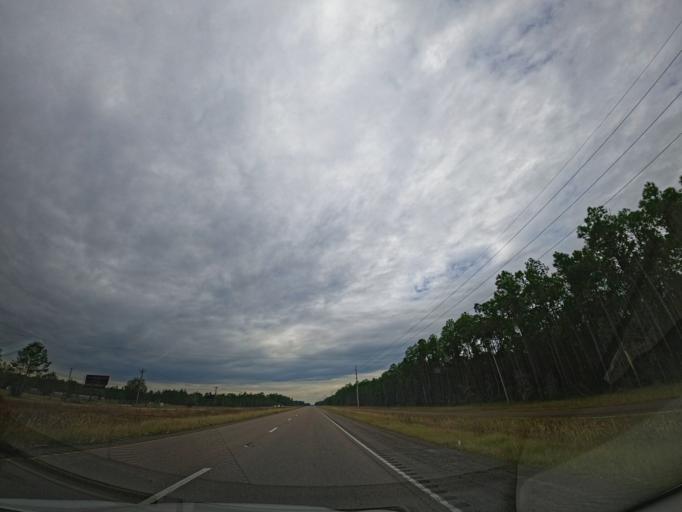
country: US
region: Mississippi
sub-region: Hancock County
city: Waveland
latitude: 30.3006
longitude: -89.4644
